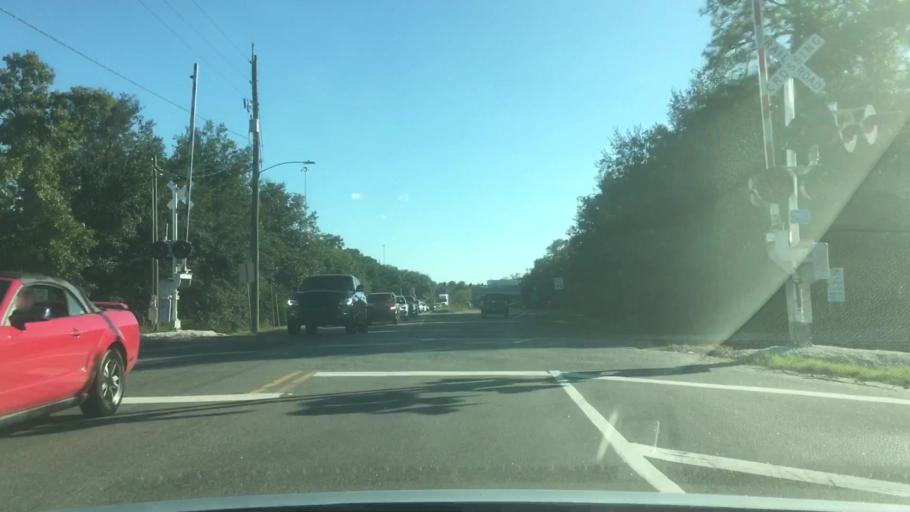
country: US
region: Florida
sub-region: Duval County
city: Jacksonville
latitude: 30.4371
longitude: -81.5797
